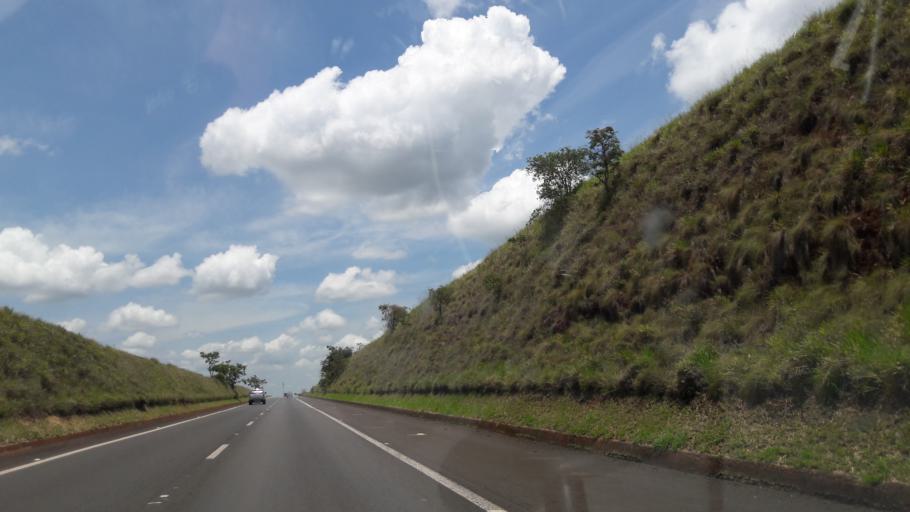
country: BR
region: Sao Paulo
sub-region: Avare
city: Avare
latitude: -22.9556
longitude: -48.8385
